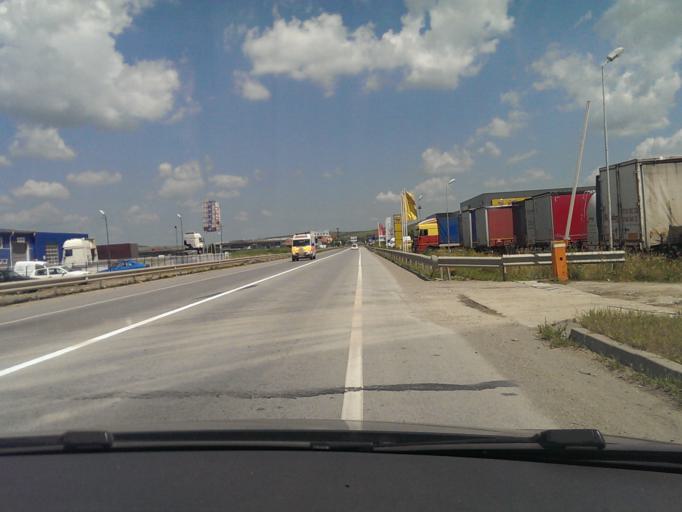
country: RO
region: Cluj
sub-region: Comuna Apahida
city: Sannicoara
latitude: 46.7826
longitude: 23.7084
